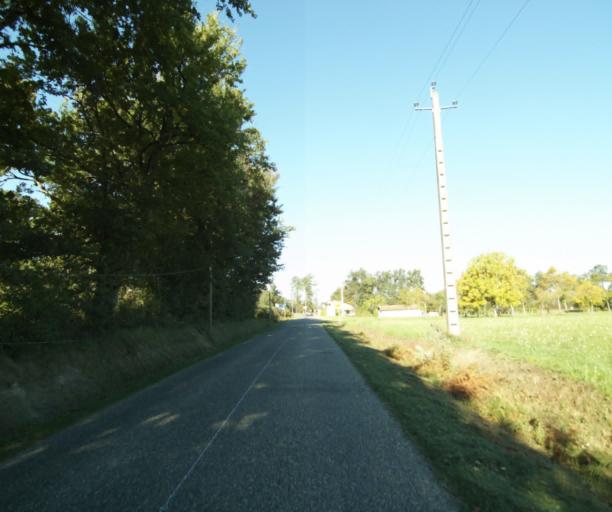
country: FR
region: Aquitaine
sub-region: Departement des Landes
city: Gabarret
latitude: 43.9560
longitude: -0.0194
